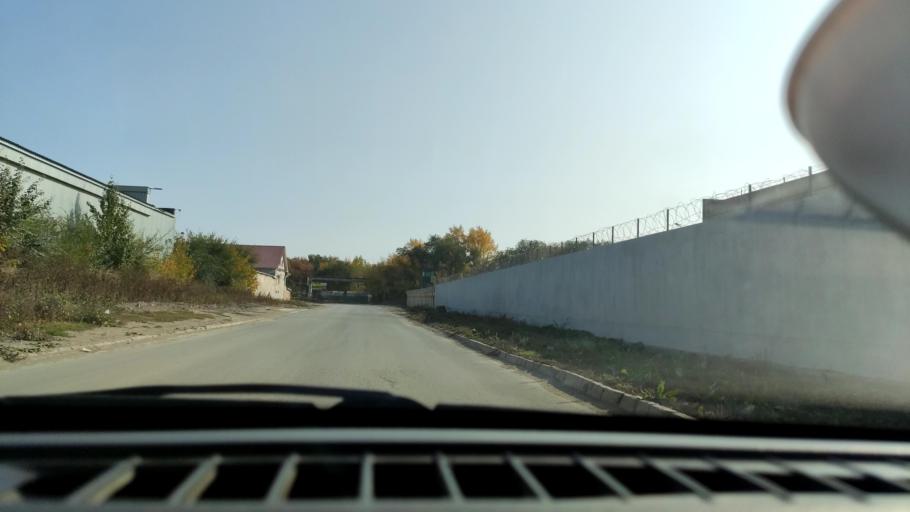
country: RU
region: Samara
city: Samara
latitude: 53.1916
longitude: 50.2650
